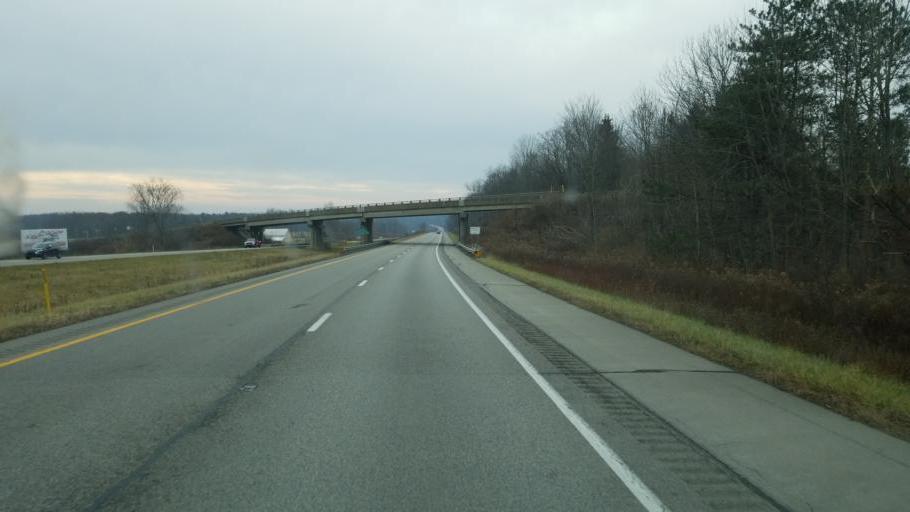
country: US
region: Pennsylvania
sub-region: Mercer County
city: Stoneboro
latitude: 41.4441
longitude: -80.1607
